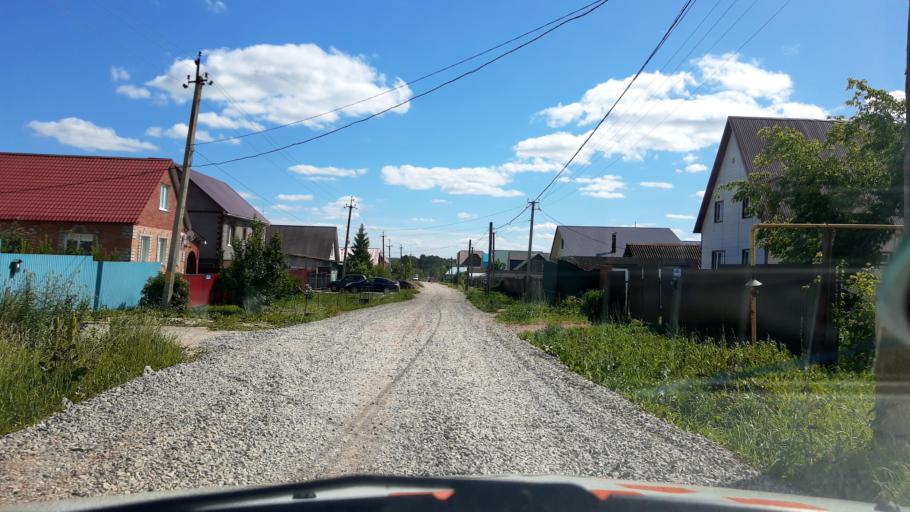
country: RU
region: Bashkortostan
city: Iglino
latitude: 54.8471
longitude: 56.4231
